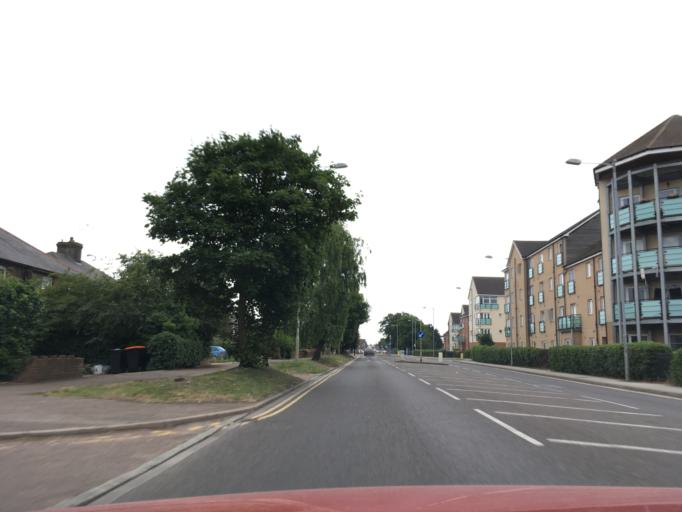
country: GB
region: England
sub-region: Central Bedfordshire
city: Dunstable
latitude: 51.8962
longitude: -0.5352
